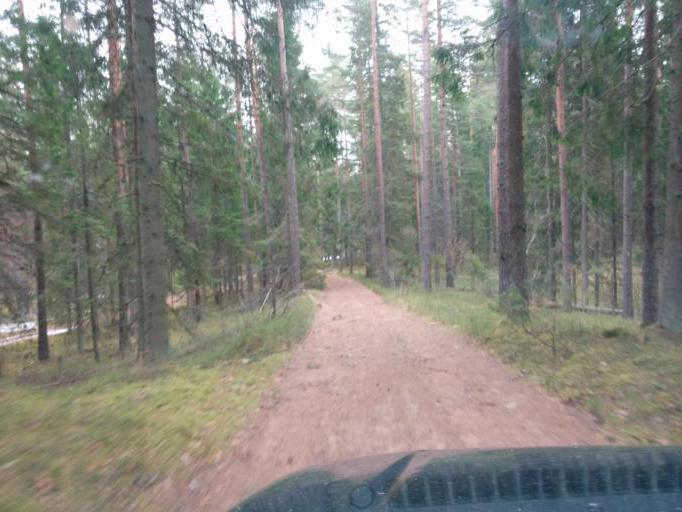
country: LV
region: Ogre
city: Ogre
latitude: 56.7494
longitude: 24.5777
